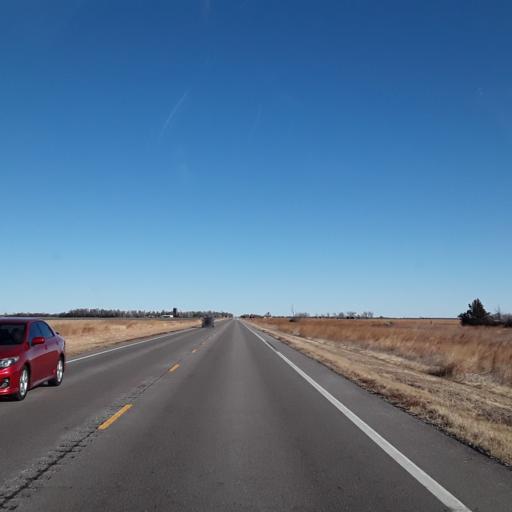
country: US
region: Kansas
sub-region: Pawnee County
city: Larned
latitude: 38.1063
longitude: -99.1990
